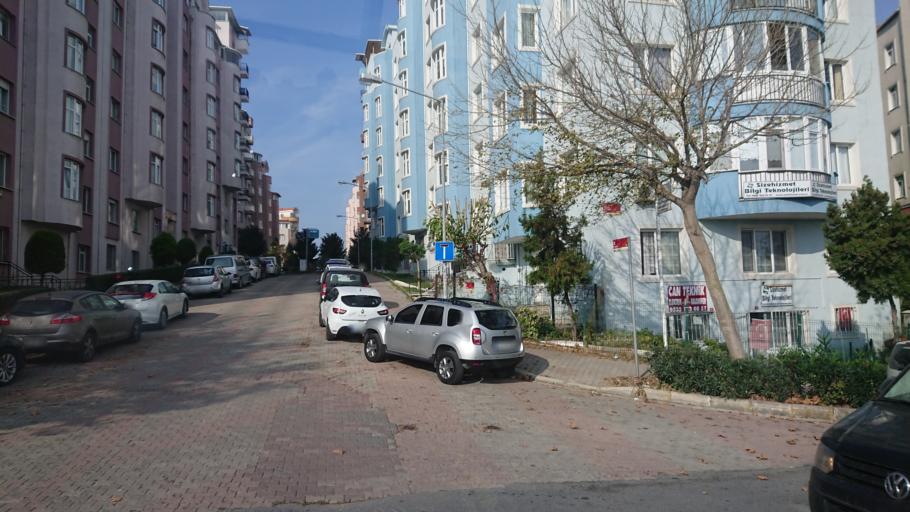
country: TR
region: Istanbul
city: Esenyurt
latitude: 41.0736
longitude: 28.6673
